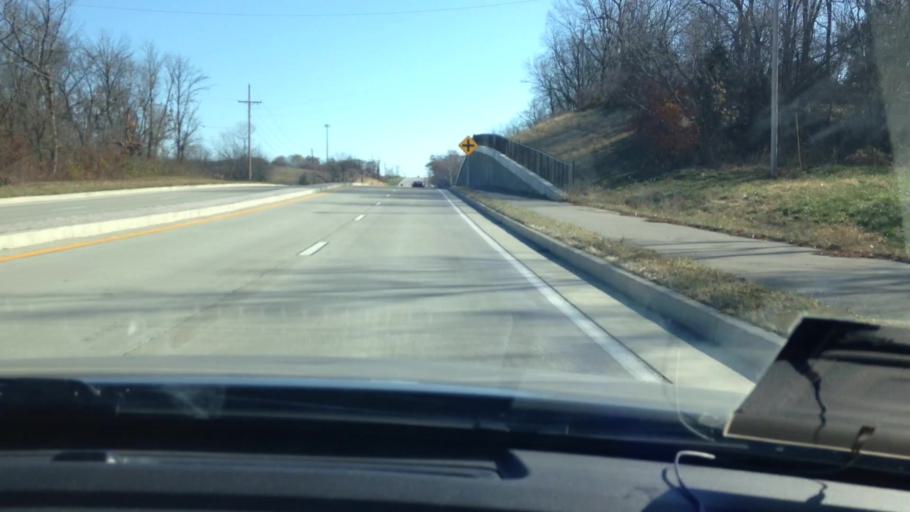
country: US
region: Missouri
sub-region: Platte County
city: Weatherby Lake
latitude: 39.2237
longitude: -94.7471
